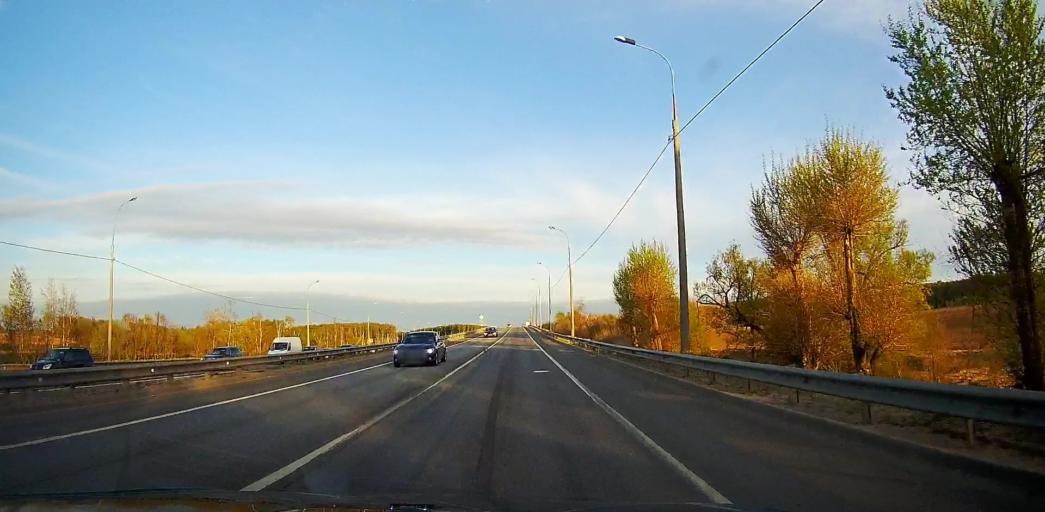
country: RU
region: Moskovskaya
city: Troitskoye
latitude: 55.2392
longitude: 38.5415
